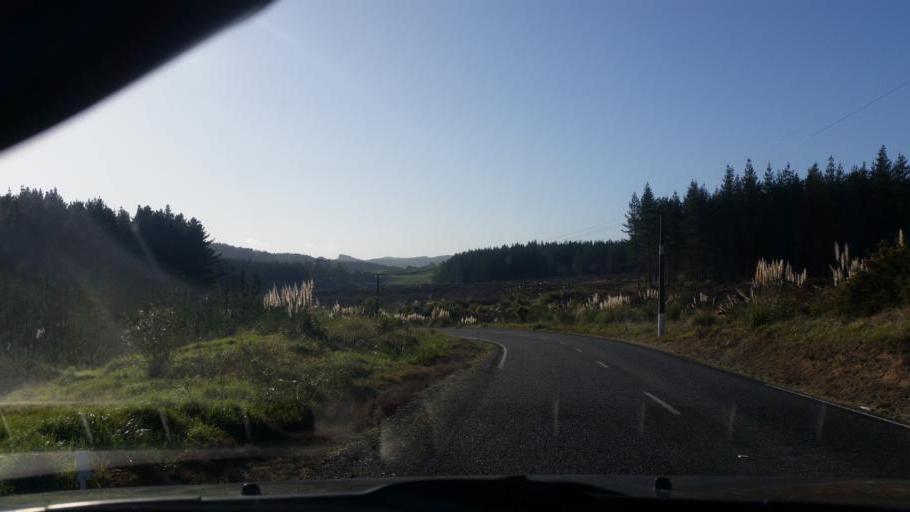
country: NZ
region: Auckland
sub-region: Auckland
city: Wellsford
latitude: -36.2202
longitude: 174.4624
